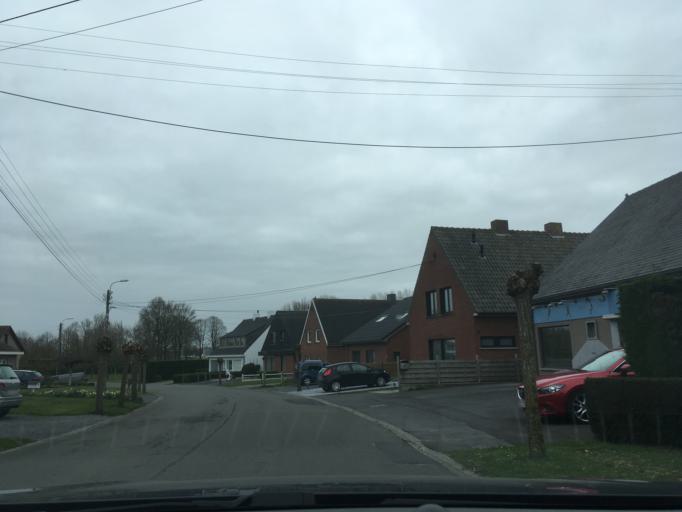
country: BE
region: Flanders
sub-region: Provincie West-Vlaanderen
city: Kortemark
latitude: 51.0281
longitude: 3.0355
